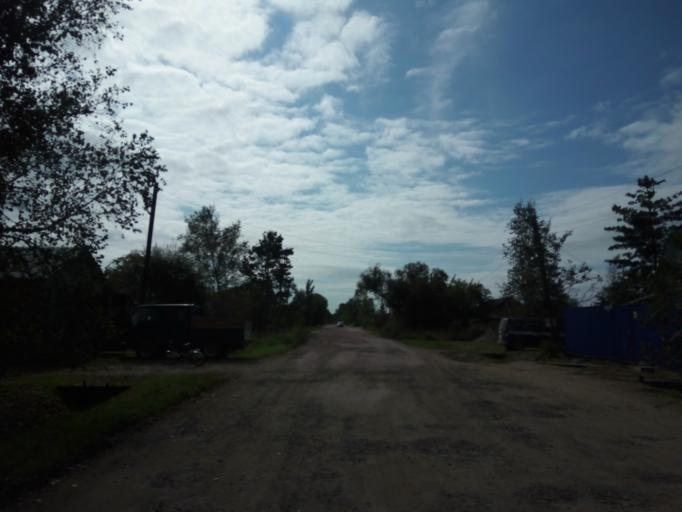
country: RU
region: Primorskiy
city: Dal'nerechensk
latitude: 45.9188
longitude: 133.7219
